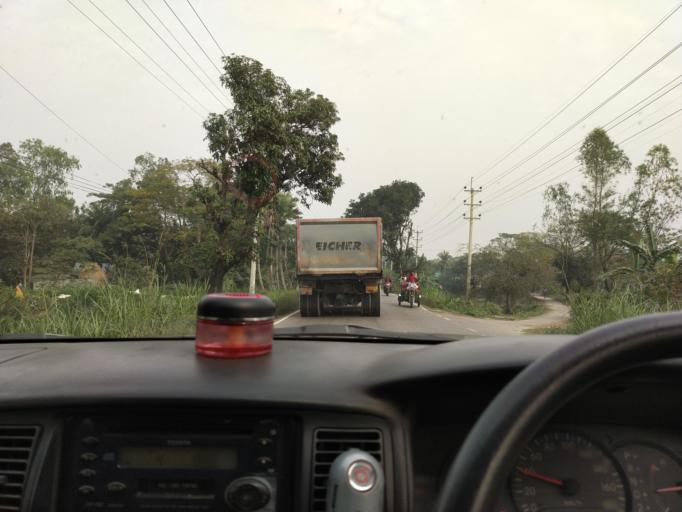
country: BD
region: Dhaka
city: Narsingdi
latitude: 24.0203
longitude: 90.7378
